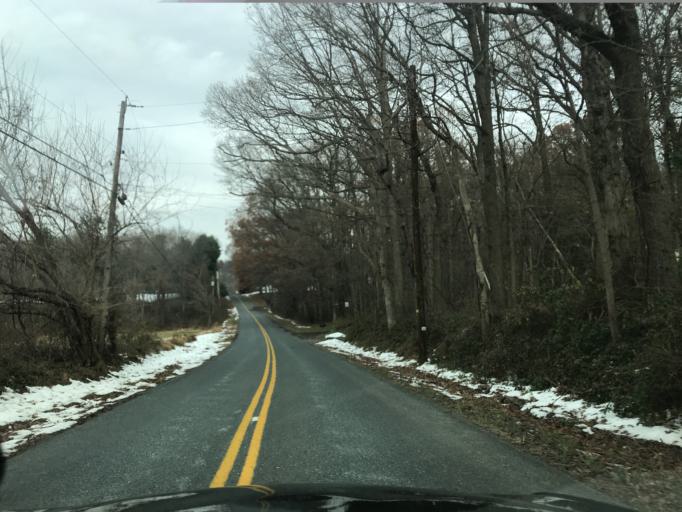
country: US
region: Pennsylvania
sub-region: York County
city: Susquehanna Trails
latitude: 39.6872
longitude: -76.4204
